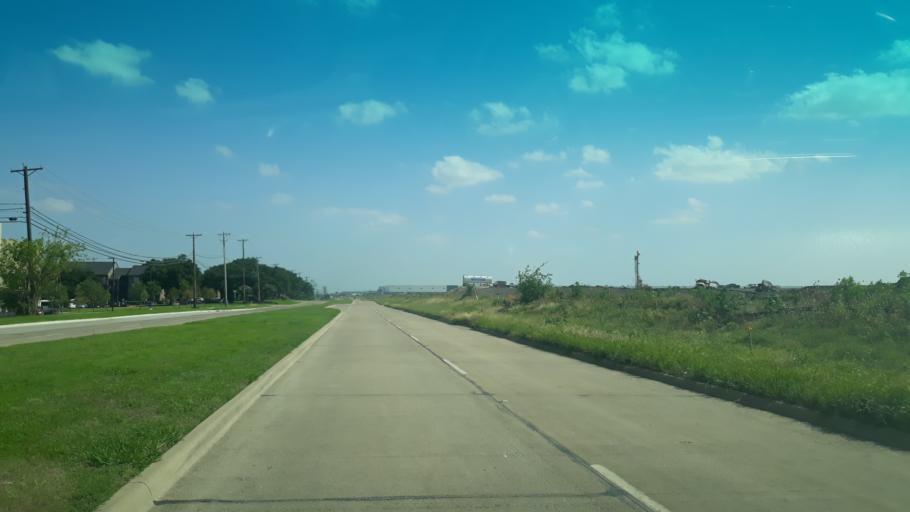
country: US
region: Texas
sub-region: Tarrant County
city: Euless
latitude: 32.8548
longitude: -97.0215
